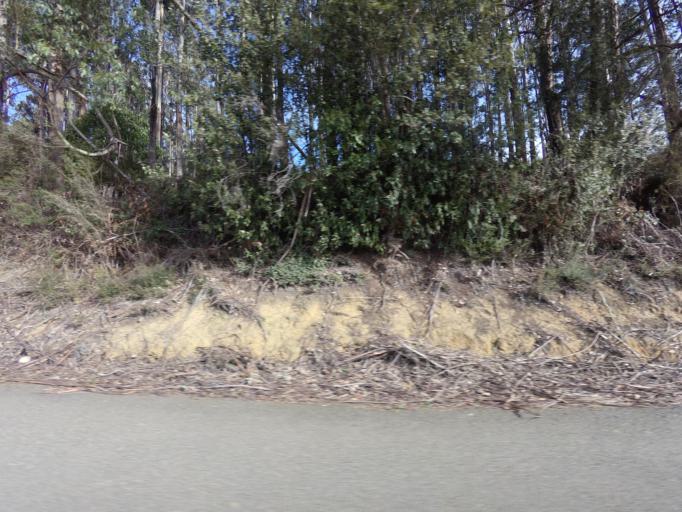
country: AU
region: Tasmania
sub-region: Kingborough
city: Margate
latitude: -43.0178
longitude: 147.1642
